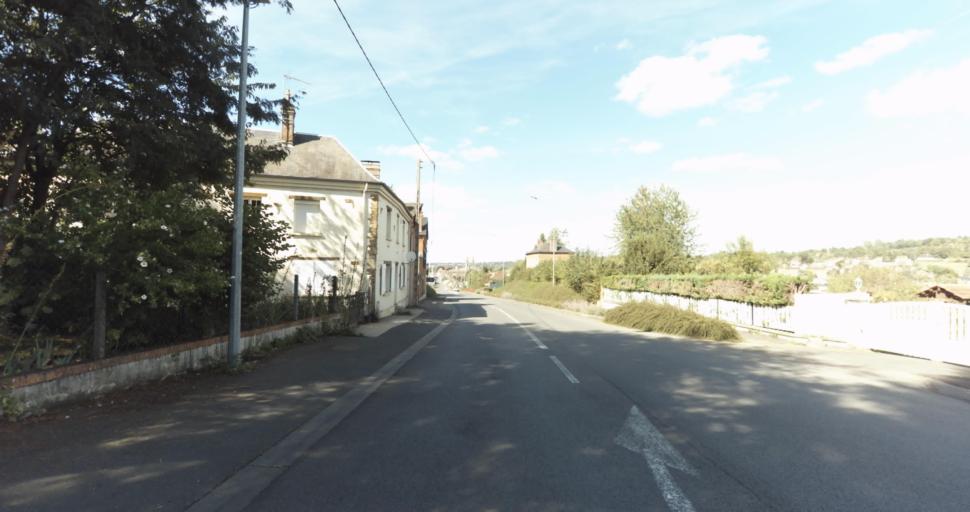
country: FR
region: Lower Normandy
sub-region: Departement de l'Orne
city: Vimoutiers
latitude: 48.9207
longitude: 0.1995
